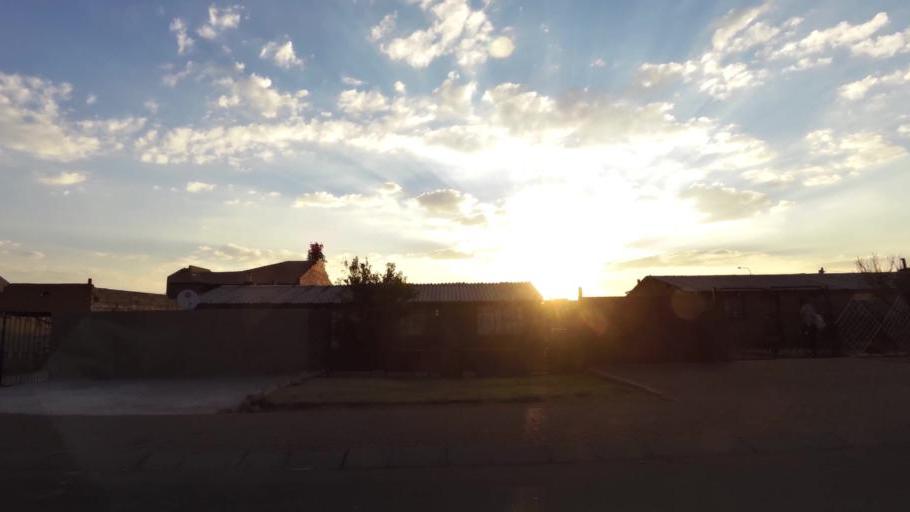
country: ZA
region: Gauteng
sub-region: City of Johannesburg Metropolitan Municipality
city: Soweto
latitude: -26.2279
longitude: 27.8972
